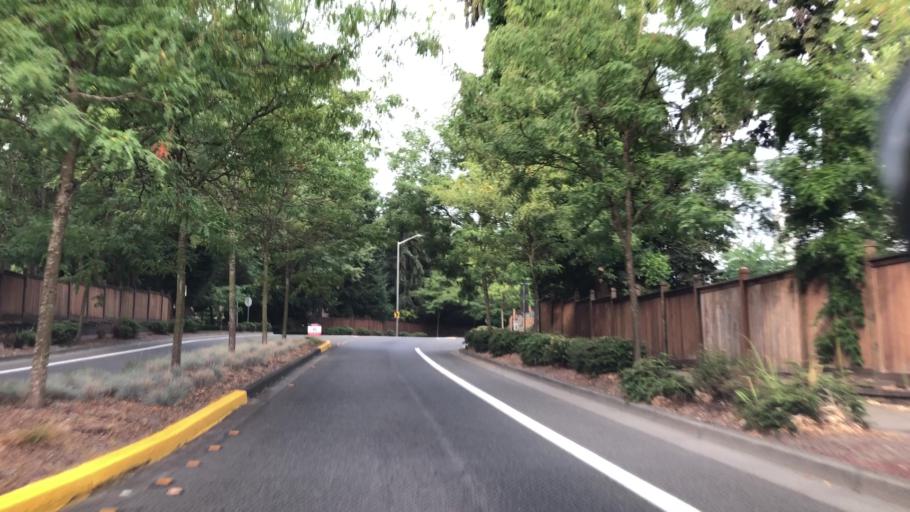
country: US
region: Washington
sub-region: King County
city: Redmond
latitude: 47.6669
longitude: -122.1600
